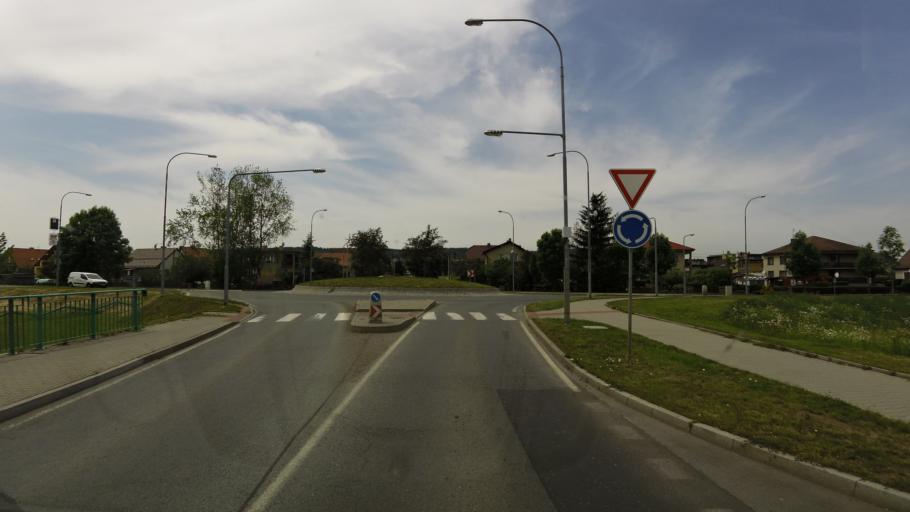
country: CZ
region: Plzensky
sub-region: Okres Rokycany
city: Rokycany
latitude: 49.7335
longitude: 13.5876
